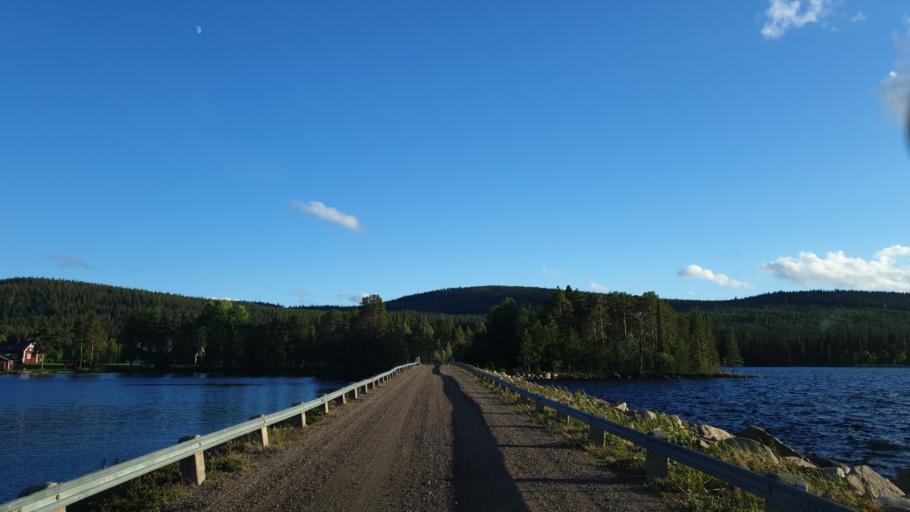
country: SE
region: Norrbotten
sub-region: Arvidsjaurs Kommun
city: Arvidsjaur
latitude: 65.7109
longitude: 18.7083
